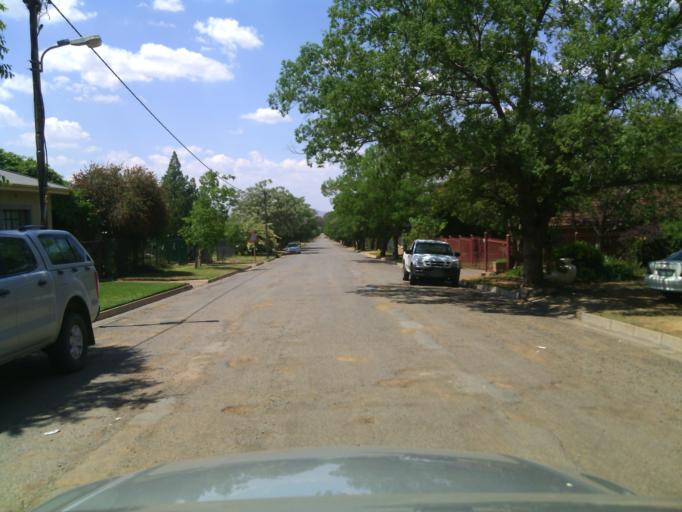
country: ZA
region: Orange Free State
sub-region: Xhariep District Municipality
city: Dewetsdorp
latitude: -29.5829
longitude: 26.6603
